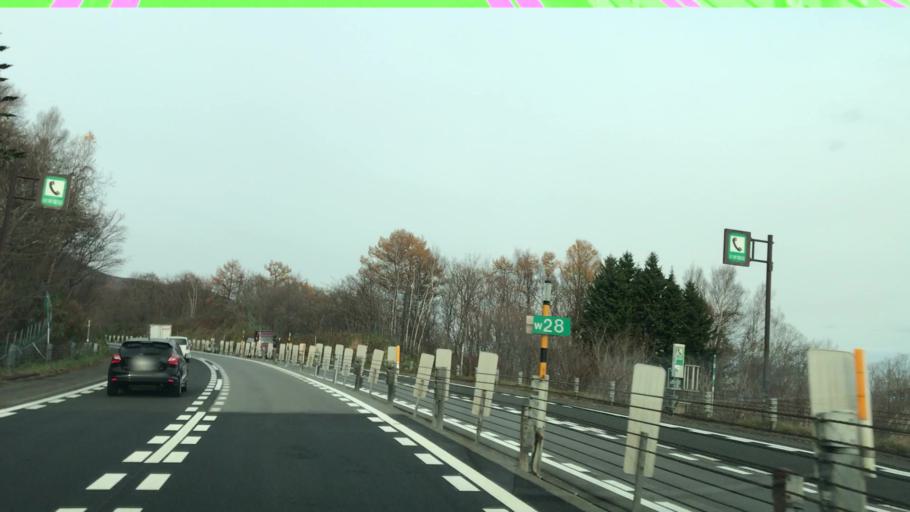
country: JP
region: Hokkaido
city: Otaru
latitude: 43.1513
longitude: 141.1268
